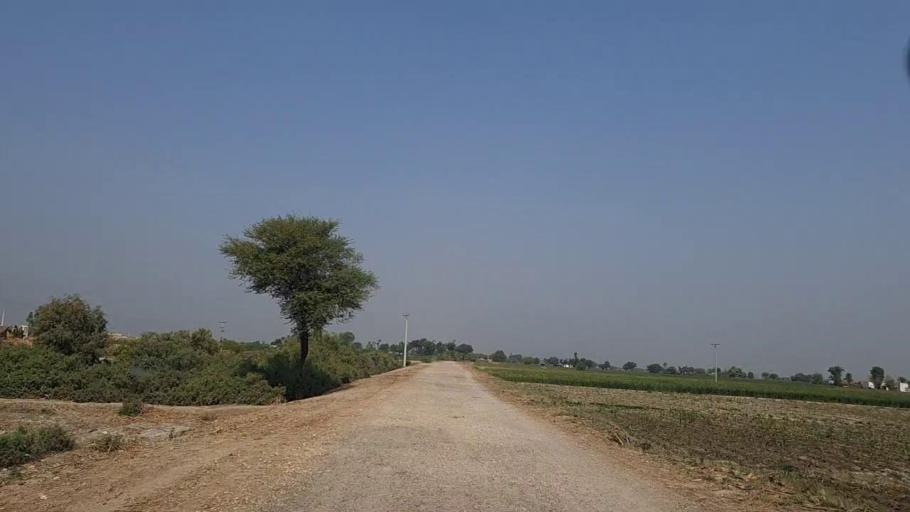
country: PK
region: Sindh
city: Mirpur Khas
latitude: 25.4967
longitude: 69.1911
